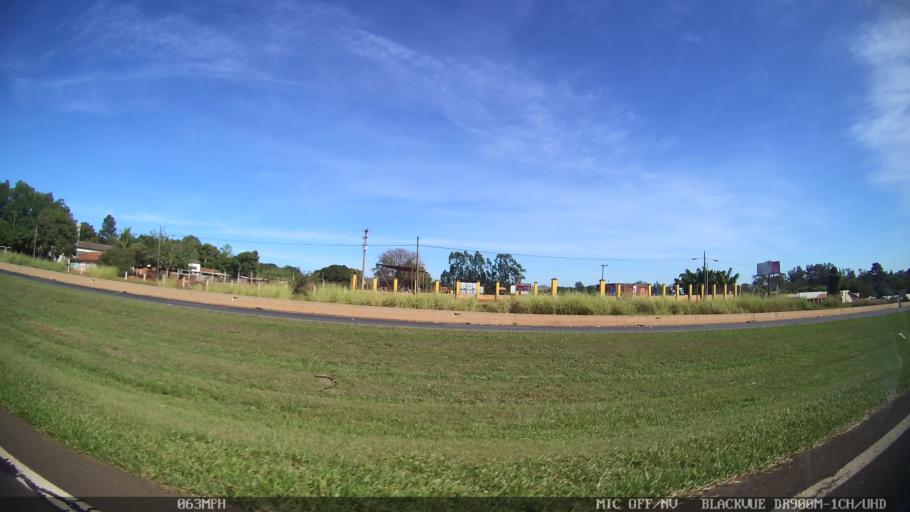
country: BR
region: Sao Paulo
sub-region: Leme
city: Leme
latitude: -22.2213
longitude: -47.3919
